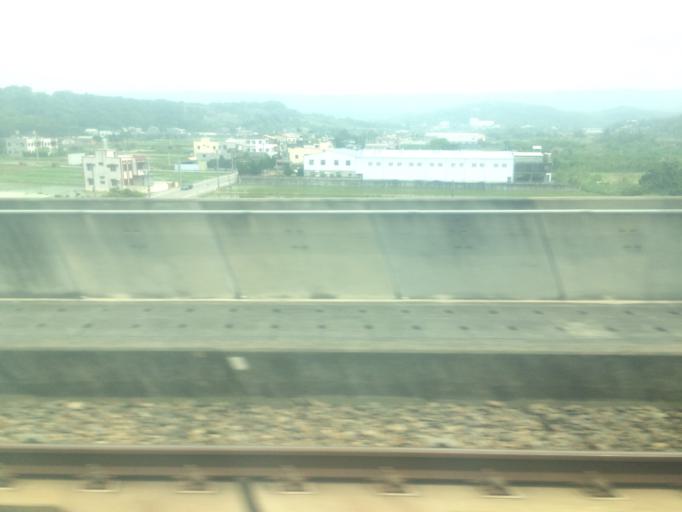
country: TW
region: Taiwan
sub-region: Miaoli
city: Miaoli
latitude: 24.4695
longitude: 120.7062
